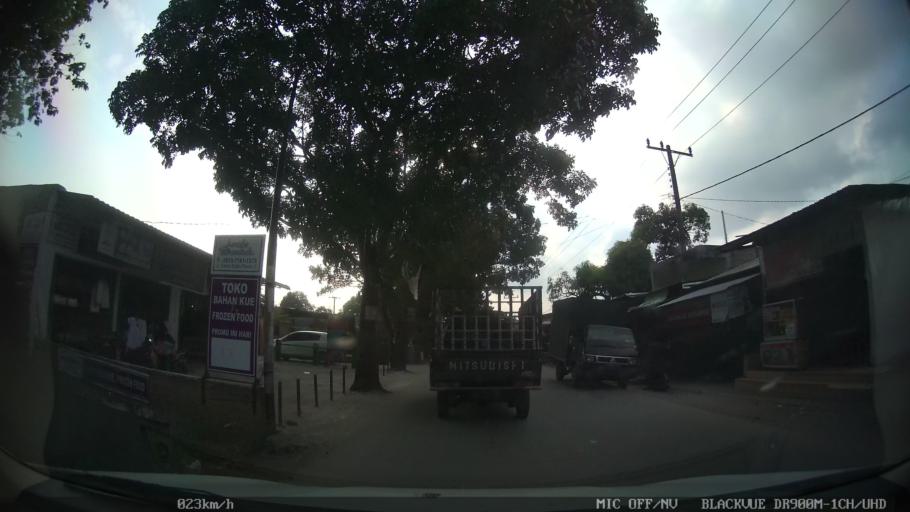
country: ID
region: North Sumatra
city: Medan
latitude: 3.5813
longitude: 98.7452
